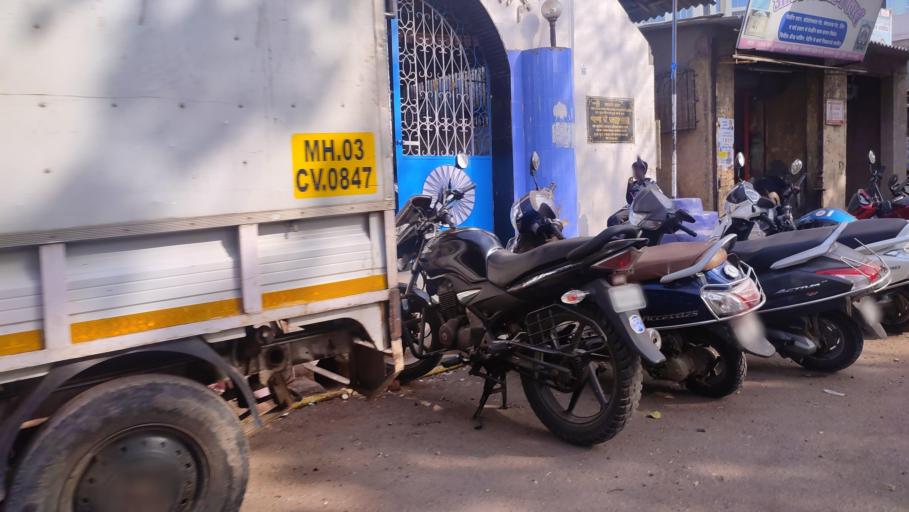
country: IN
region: Maharashtra
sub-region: Mumbai Suburban
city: Mumbai
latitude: 19.0744
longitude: 72.9127
